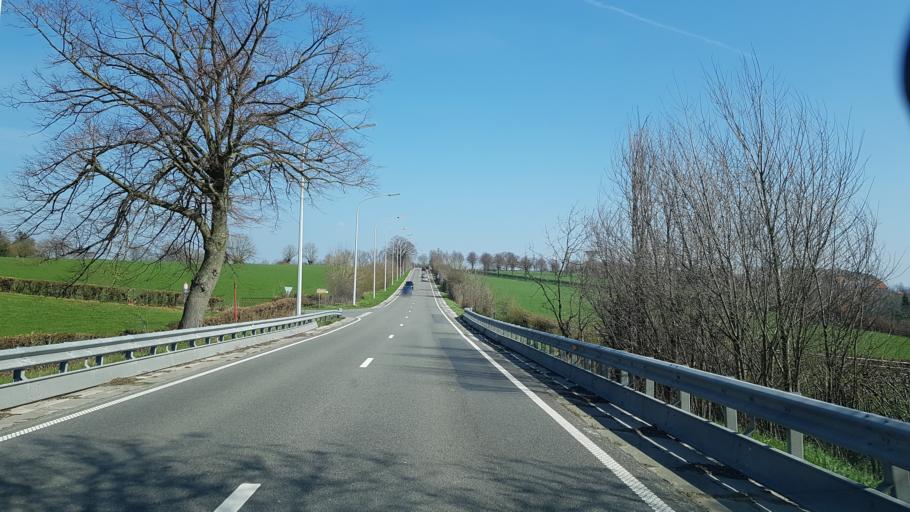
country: BE
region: Wallonia
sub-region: Province de Liege
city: Aubel
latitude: 50.6706
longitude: 5.9047
